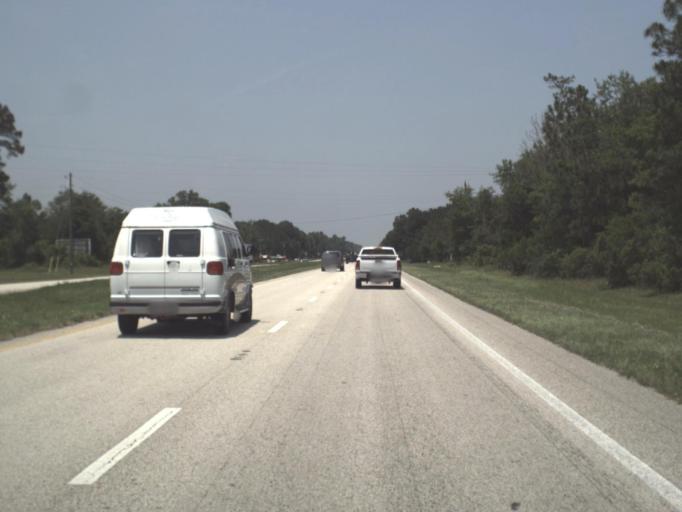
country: US
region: Florida
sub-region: Duval County
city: Baldwin
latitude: 30.1818
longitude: -82.0222
